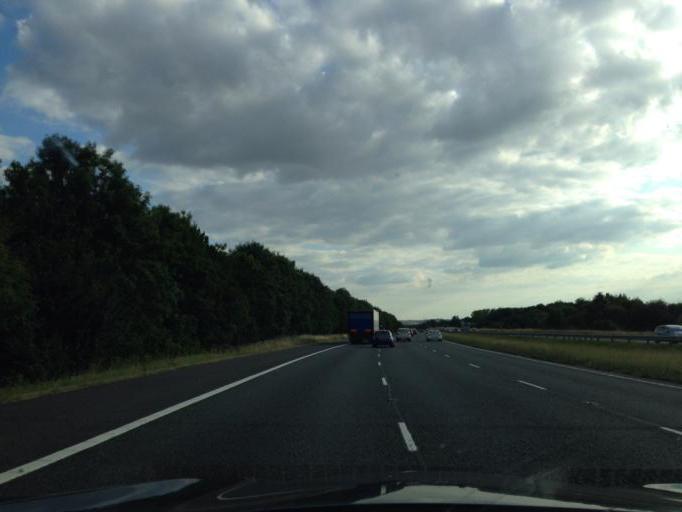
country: GB
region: England
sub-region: Oxfordshire
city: Wheatley
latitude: 51.7883
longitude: -1.0867
